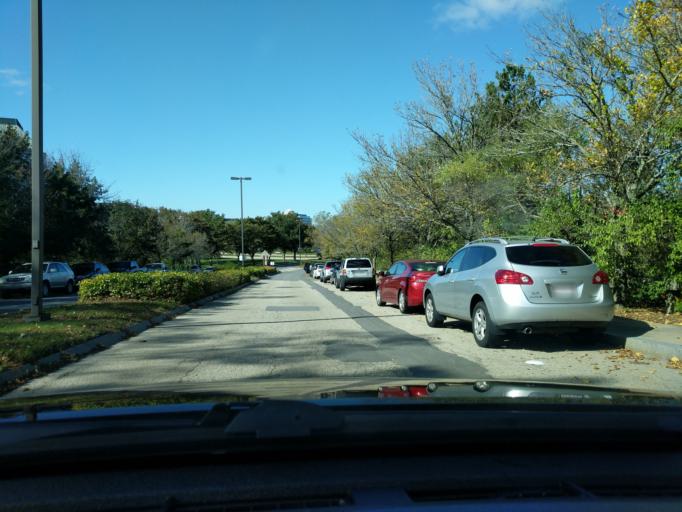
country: US
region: Massachusetts
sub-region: Norfolk County
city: Braintree
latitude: 42.2299
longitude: -71.0160
